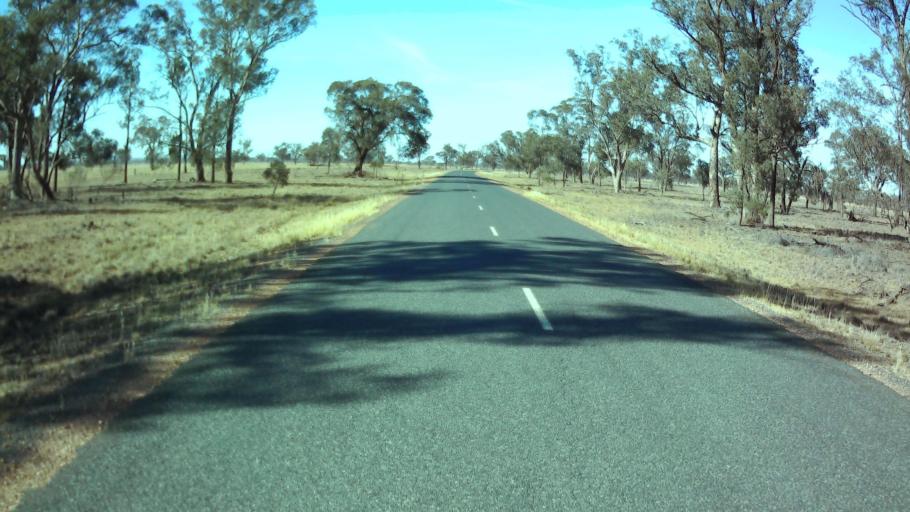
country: AU
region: New South Wales
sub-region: Weddin
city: Grenfell
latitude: -34.0674
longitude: 147.9061
